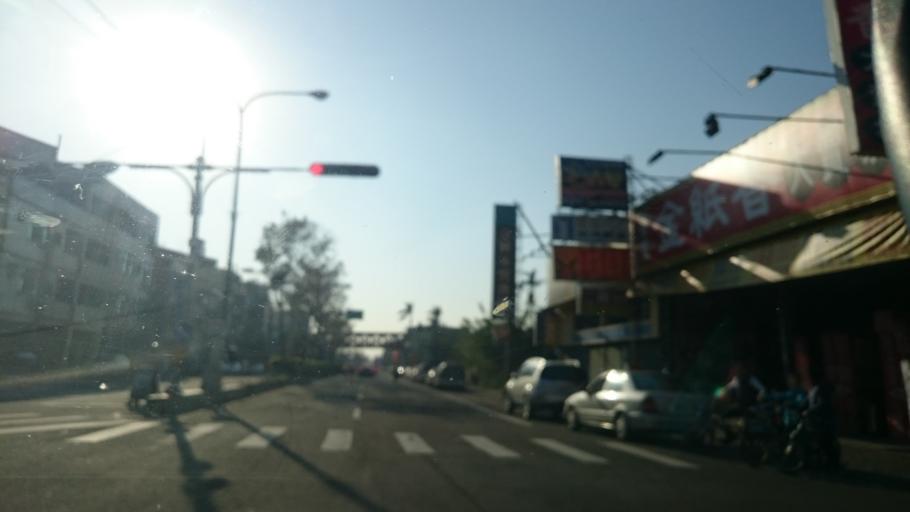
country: TW
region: Taiwan
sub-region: Hsinchu
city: Hsinchu
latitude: 24.6856
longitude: 120.9032
